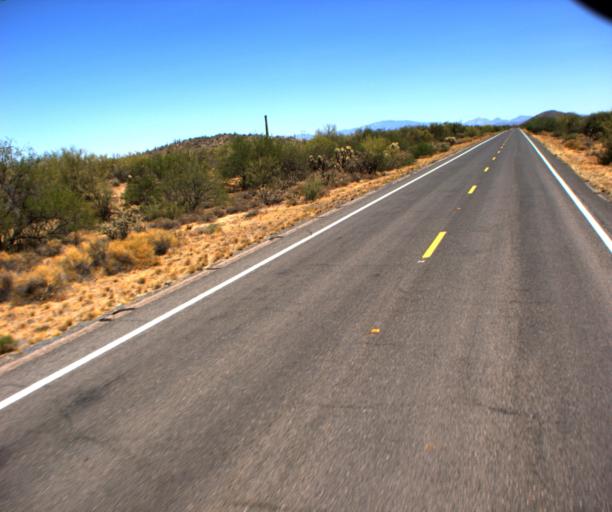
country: US
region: Arizona
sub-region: Pinal County
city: Florence
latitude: 32.7855
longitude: -111.1701
